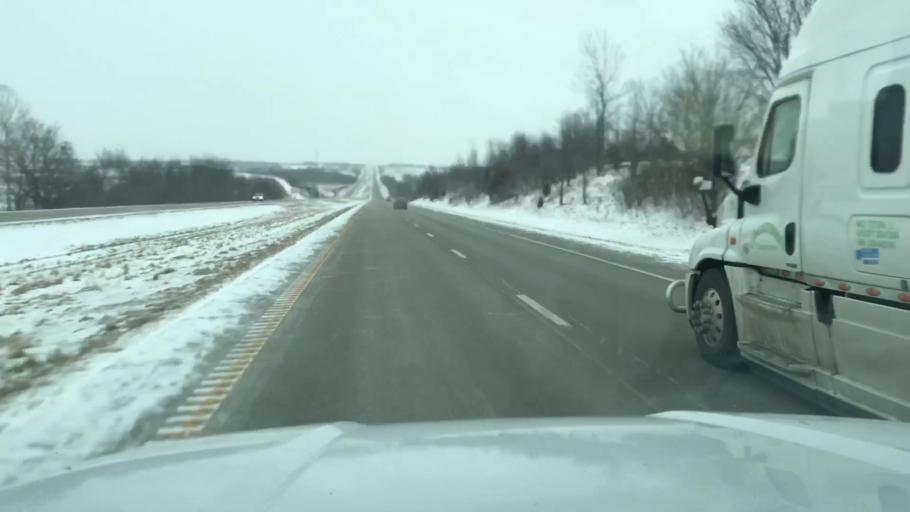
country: US
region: Missouri
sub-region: Clinton County
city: Gower
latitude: 39.7475
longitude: -94.6804
